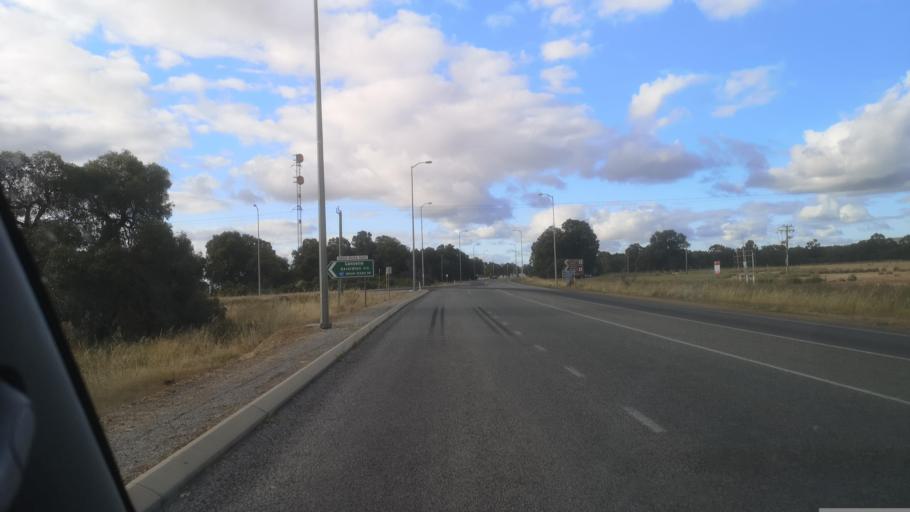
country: AU
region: Western Australia
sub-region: Wanneroo
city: Yanchep
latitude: -31.3335
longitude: 115.8683
